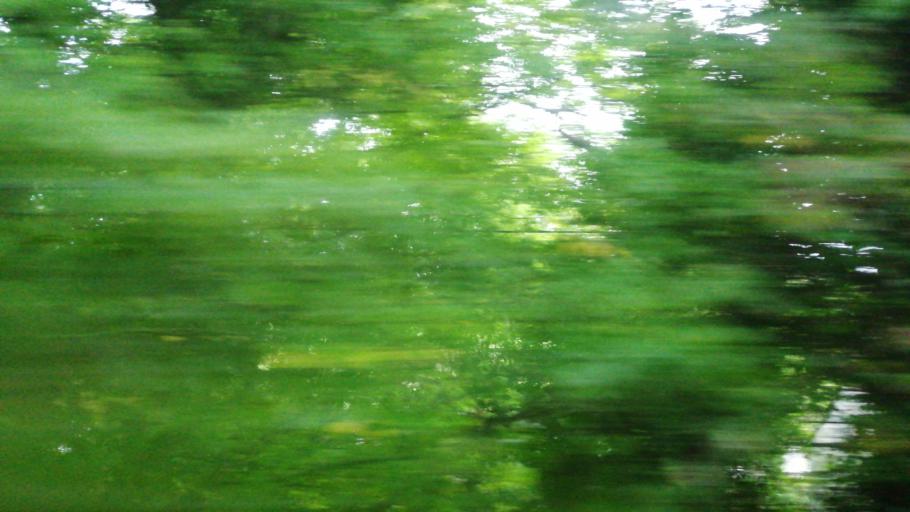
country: GB
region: Scotland
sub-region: Highland
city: Golspie
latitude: 57.9852
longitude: -3.9508
